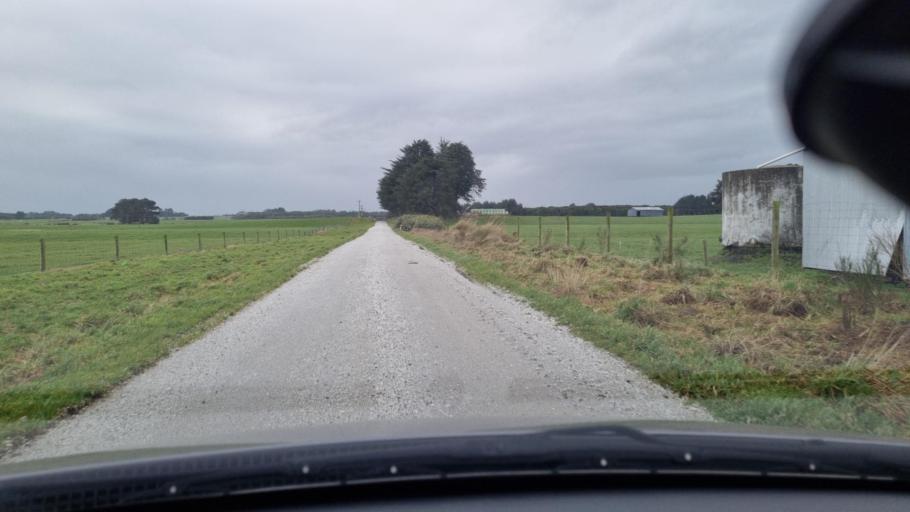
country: NZ
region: Southland
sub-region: Invercargill City
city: Invercargill
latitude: -46.4489
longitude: 168.4205
